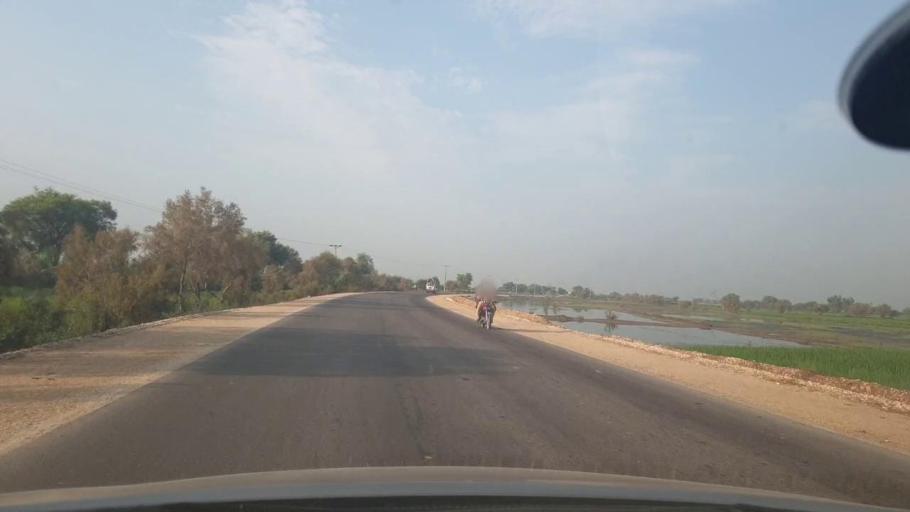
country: PK
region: Sindh
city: Jacobabad
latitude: 28.2390
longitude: 68.3918
